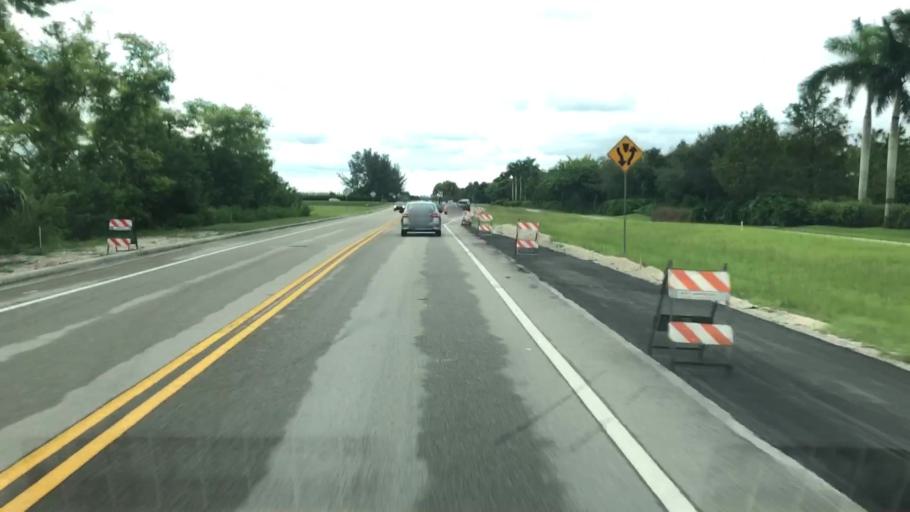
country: US
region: Florida
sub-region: Broward County
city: Parkland
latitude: 26.3344
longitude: -80.2708
